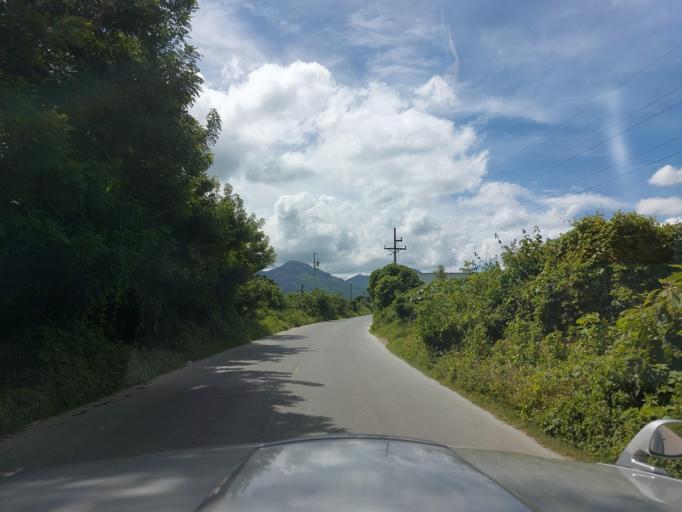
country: GT
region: Chimaltenango
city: Parramos
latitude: 14.6156
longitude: -90.8229
